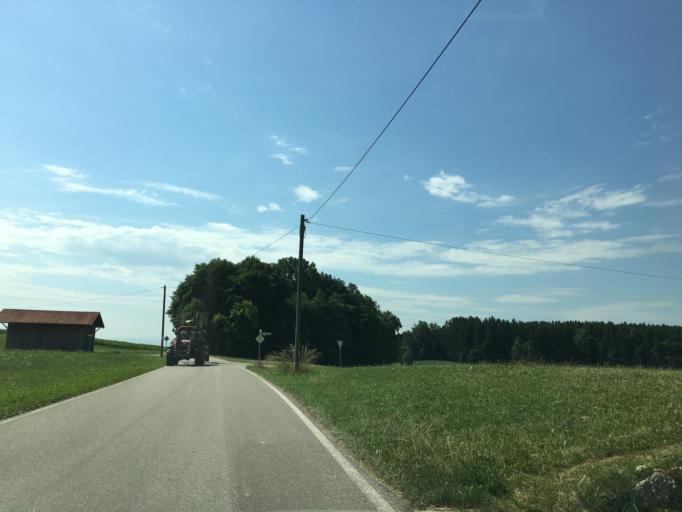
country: DE
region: Bavaria
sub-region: Upper Bavaria
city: Albaching
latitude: 48.1079
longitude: 12.0918
